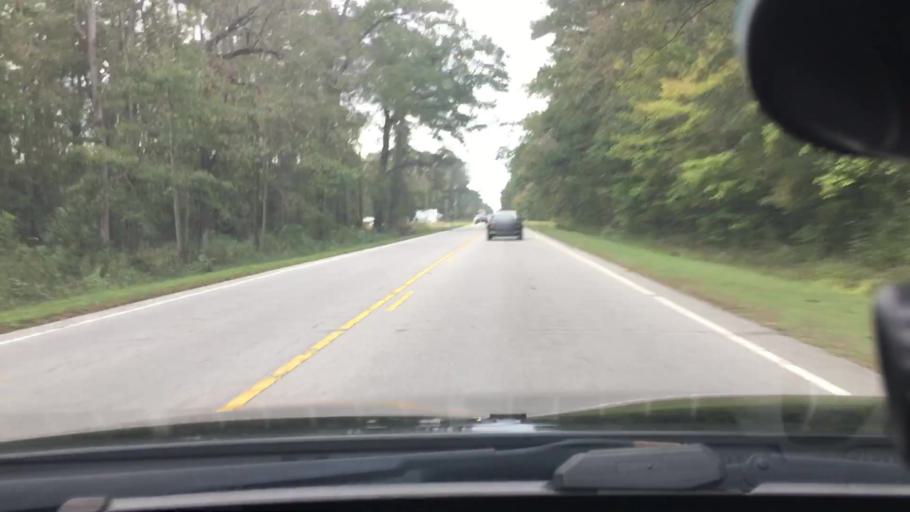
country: US
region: North Carolina
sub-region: Craven County
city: Vanceboro
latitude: 35.2630
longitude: -77.1035
